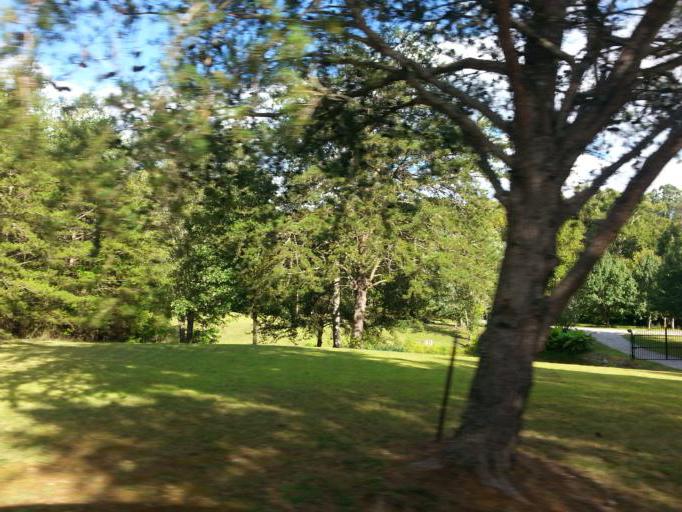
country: US
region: Tennessee
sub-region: Knox County
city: Mascot
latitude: 36.1075
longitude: -83.7852
